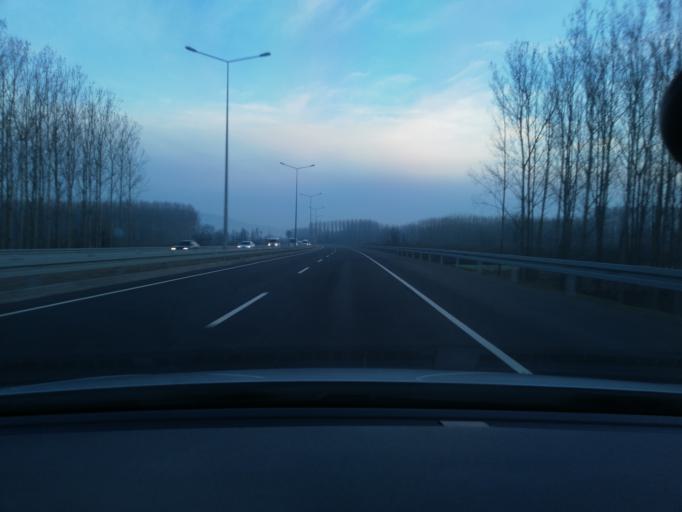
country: TR
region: Duzce
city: Duzce
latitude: 40.8089
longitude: 31.1689
